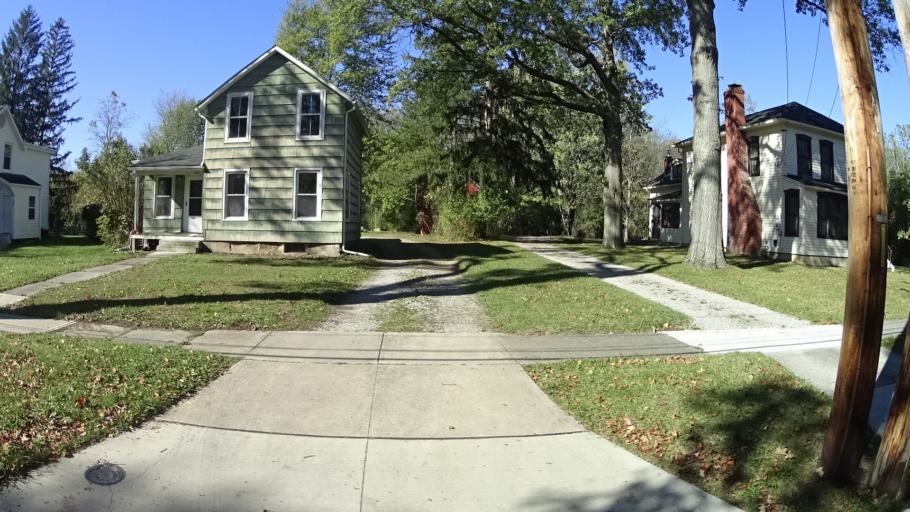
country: US
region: Ohio
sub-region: Lorain County
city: Oberlin
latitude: 41.2831
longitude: -82.2204
